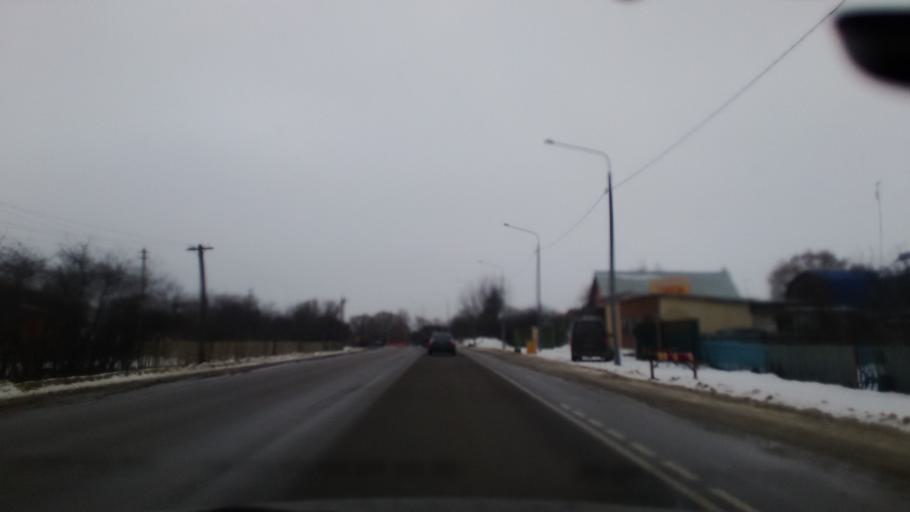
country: RU
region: Tula
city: Borodinskiy
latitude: 54.0264
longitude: 37.8898
